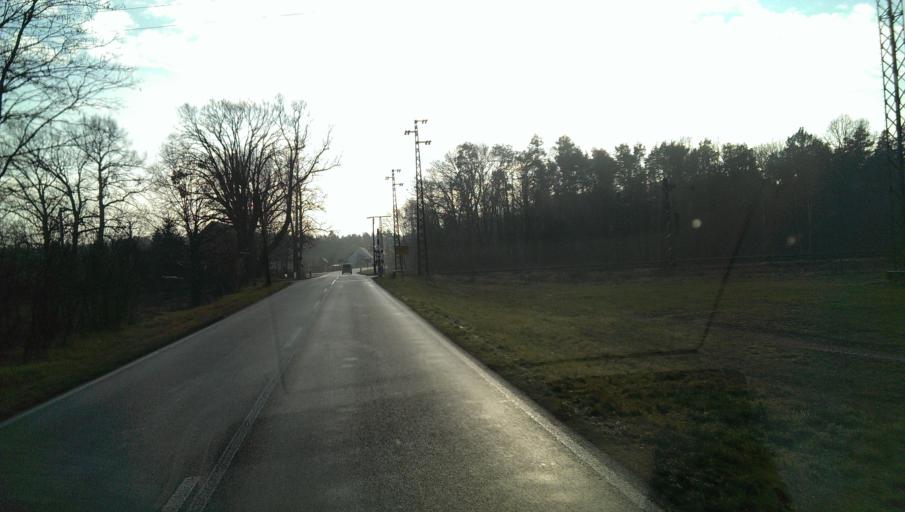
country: DE
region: Brandenburg
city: Schilda
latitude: 51.5906
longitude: 13.3575
